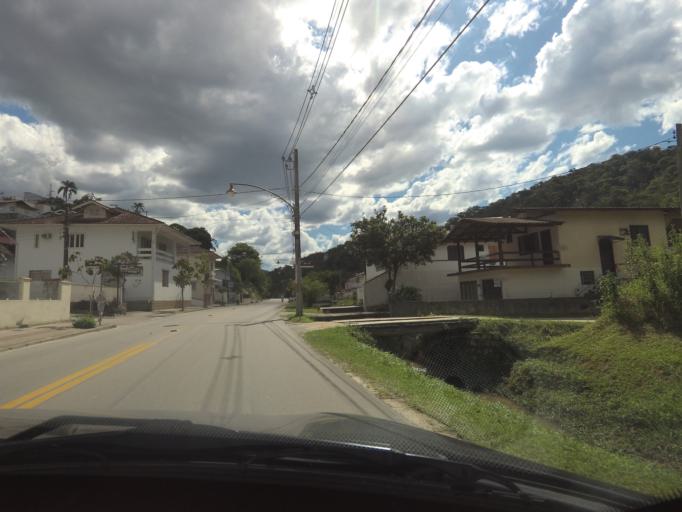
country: BR
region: Santa Catarina
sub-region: Brusque
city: Brusque
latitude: -27.0713
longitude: -48.9280
